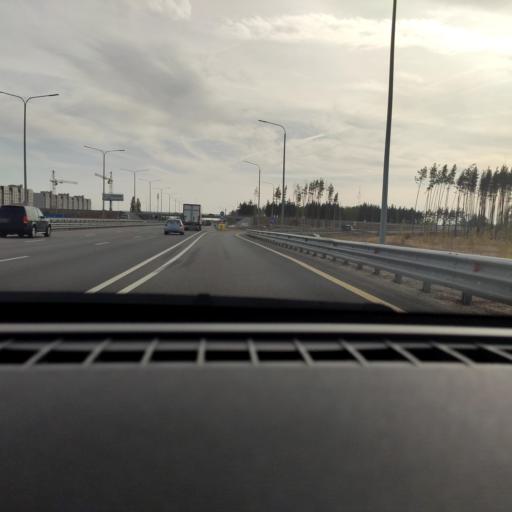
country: RU
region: Voronezj
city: Somovo
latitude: 51.7450
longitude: 39.3062
